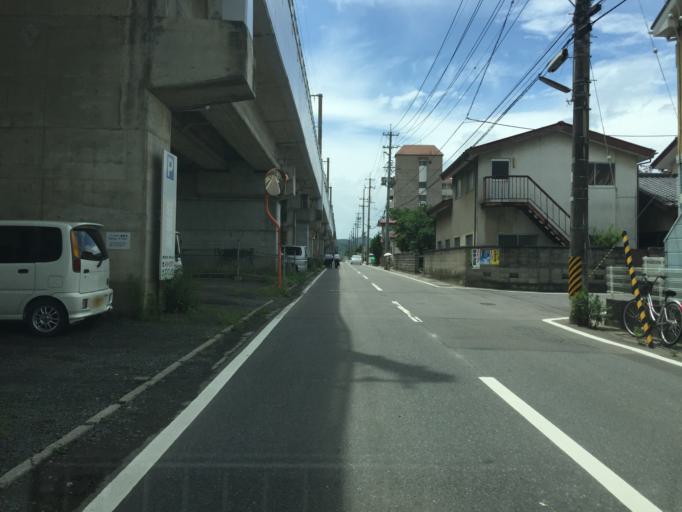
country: JP
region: Fukushima
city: Fukushima-shi
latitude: 37.7267
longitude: 140.4561
